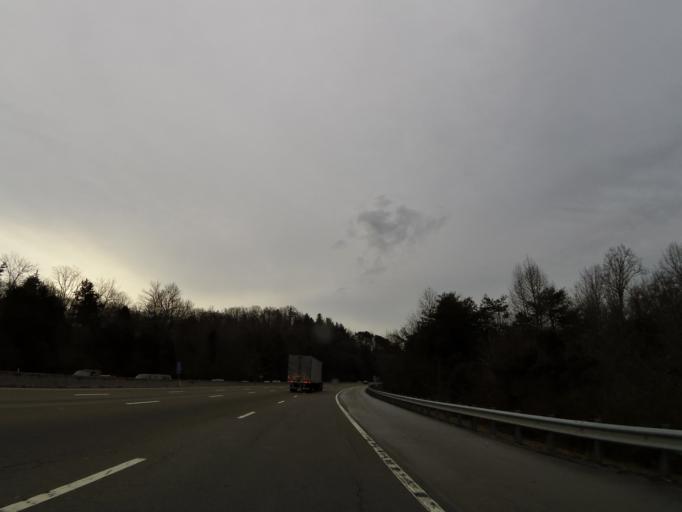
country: US
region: Tennessee
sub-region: Knox County
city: Knoxville
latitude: 36.0283
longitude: -83.9976
